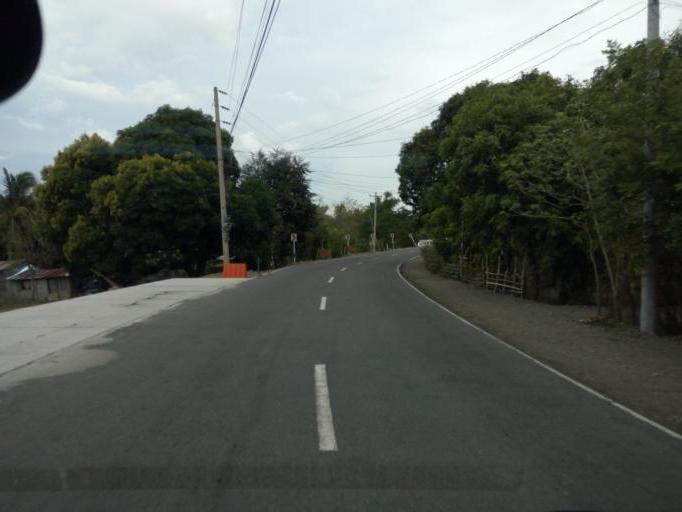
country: PH
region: Central Luzon
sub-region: Province of Nueva Ecija
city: Parista
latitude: 15.8425
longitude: 120.9358
